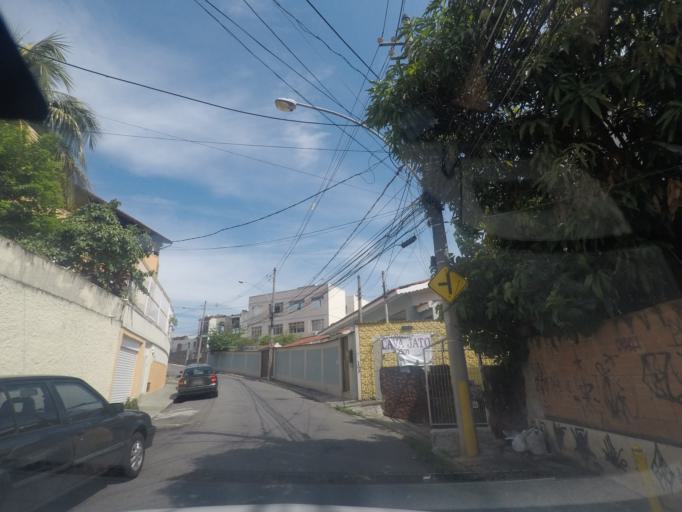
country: BR
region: Rio de Janeiro
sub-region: Rio De Janeiro
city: Rio de Janeiro
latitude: -22.8179
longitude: -43.1990
